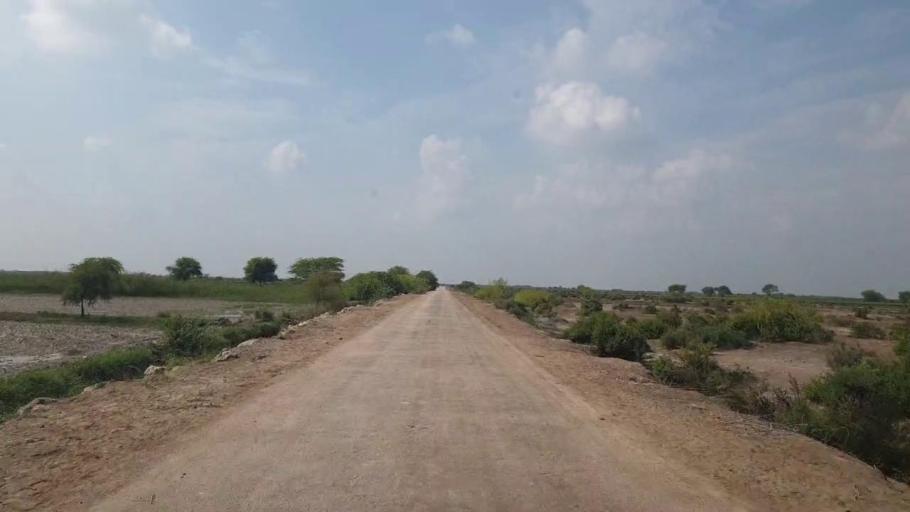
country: PK
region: Sindh
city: Badin
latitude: 24.5065
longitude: 68.6198
